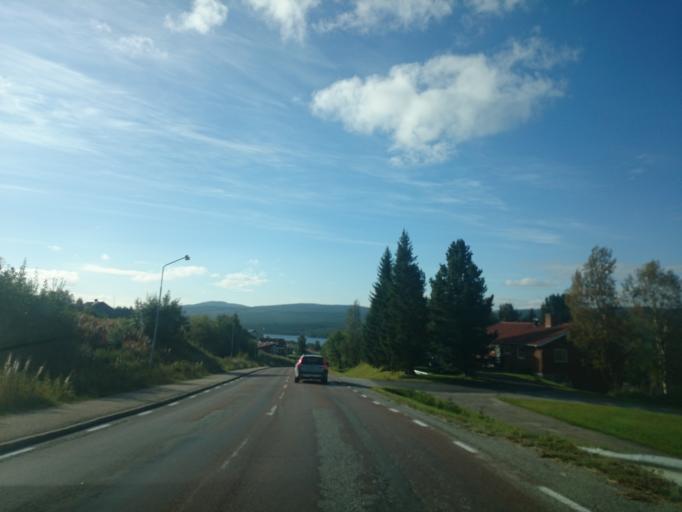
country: NO
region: Hedmark
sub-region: Engerdal
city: Engerdal
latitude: 62.5443
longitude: 12.5486
